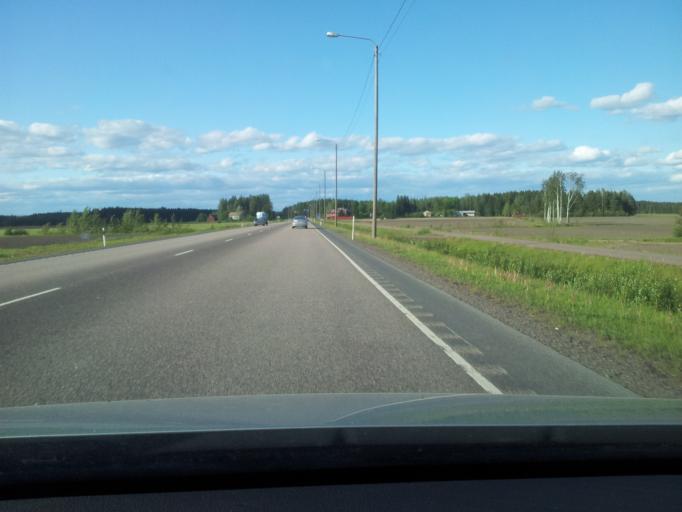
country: FI
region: Kymenlaakso
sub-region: Kouvola
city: Elimaeki
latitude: 60.8209
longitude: 26.5316
